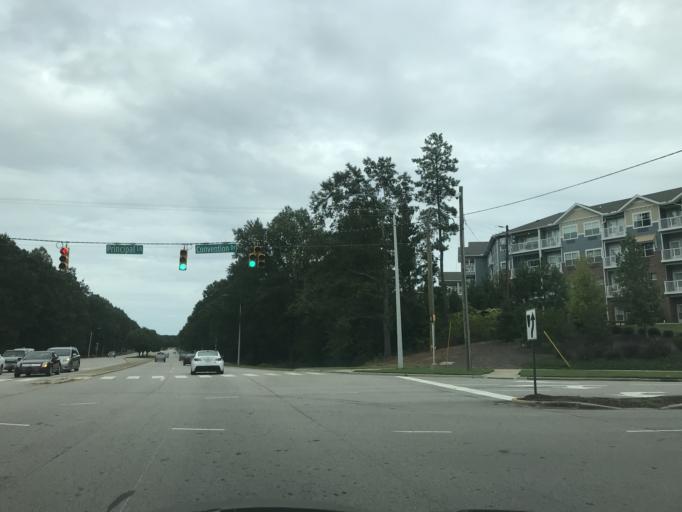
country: US
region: North Carolina
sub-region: Wake County
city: Cary
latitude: 35.7761
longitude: -78.7604
